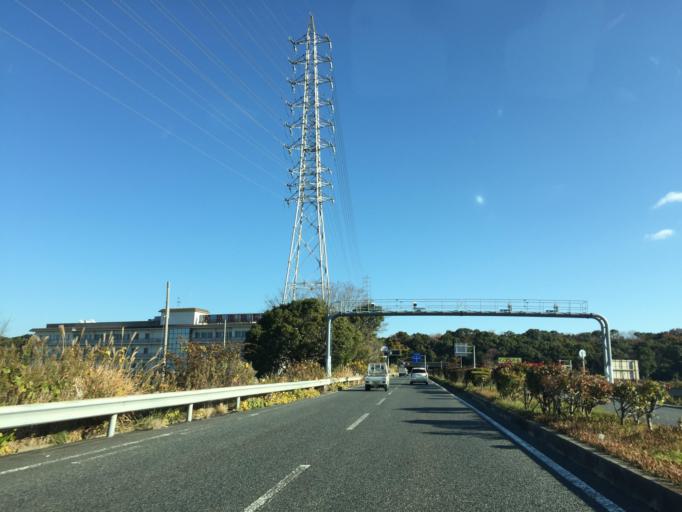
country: JP
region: Wakayama
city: Iwade
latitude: 34.3576
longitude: 135.2657
